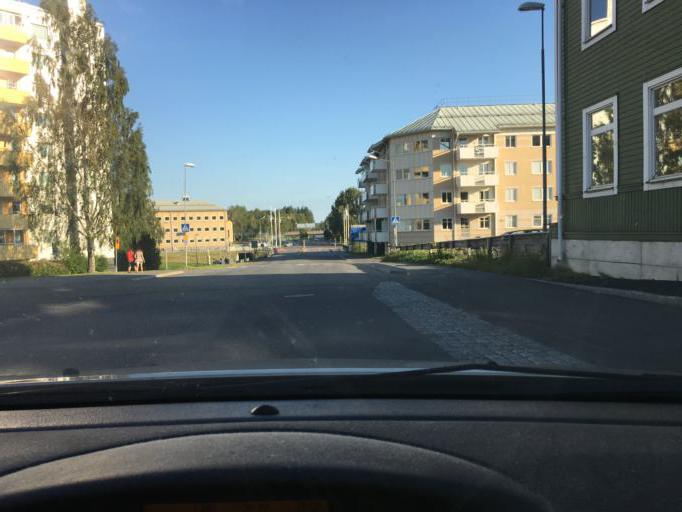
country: SE
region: Norrbotten
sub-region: Bodens Kommun
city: Boden
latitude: 65.8243
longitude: 21.6892
